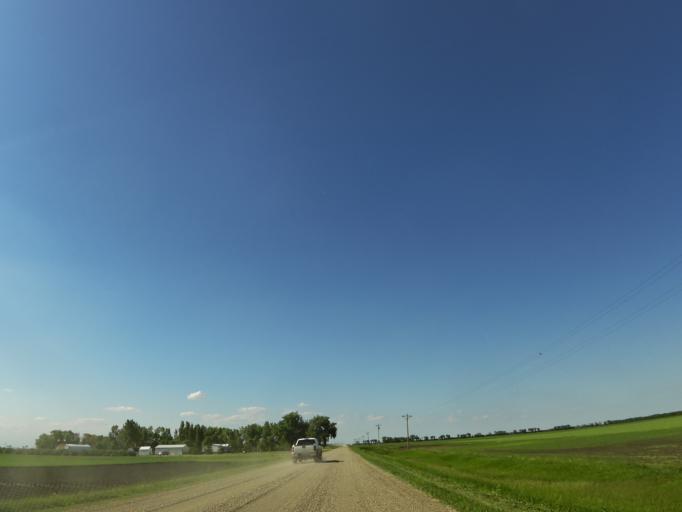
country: US
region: North Dakota
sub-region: Walsh County
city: Grafton
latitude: 48.3172
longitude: -97.2552
